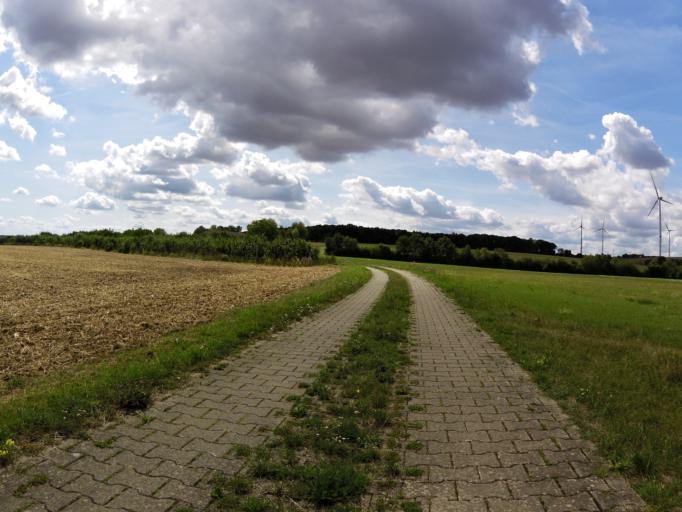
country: DE
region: Bavaria
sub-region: Regierungsbezirk Unterfranken
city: Margetshochheim
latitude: 49.8353
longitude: 9.8478
